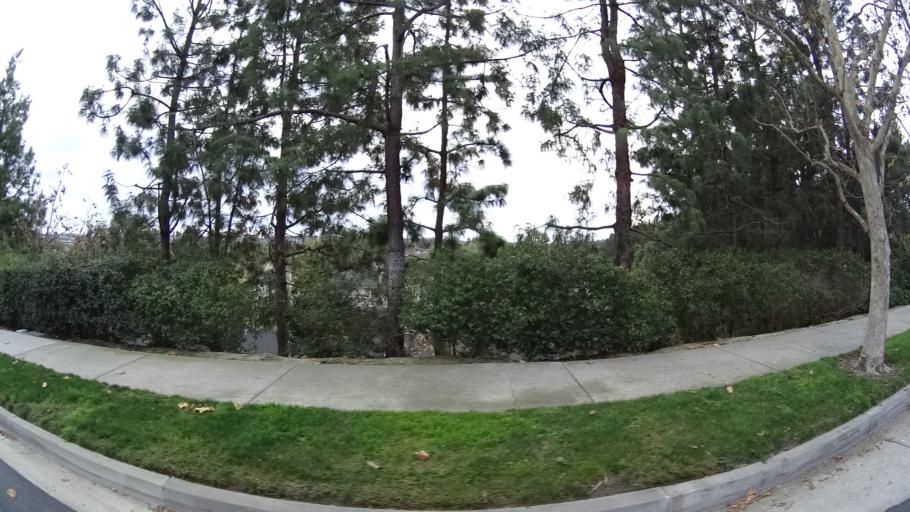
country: US
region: California
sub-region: Orange County
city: Aliso Viejo
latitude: 33.5709
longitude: -117.7228
